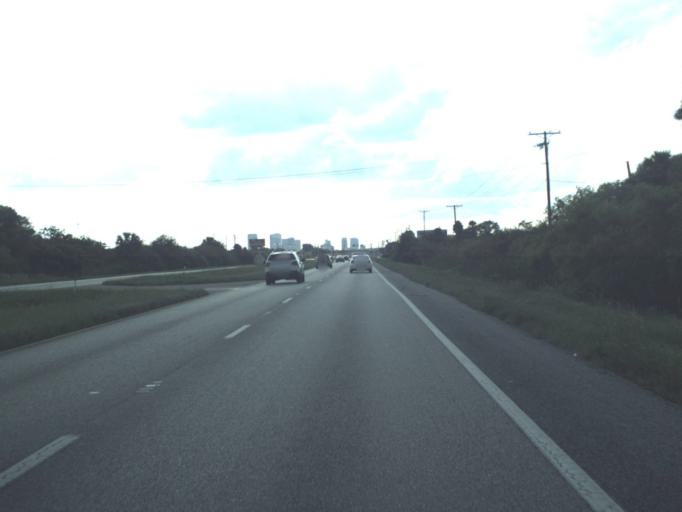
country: US
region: Florida
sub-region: Hillsborough County
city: Palm River-Clair Mel
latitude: 27.9522
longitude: -82.3926
